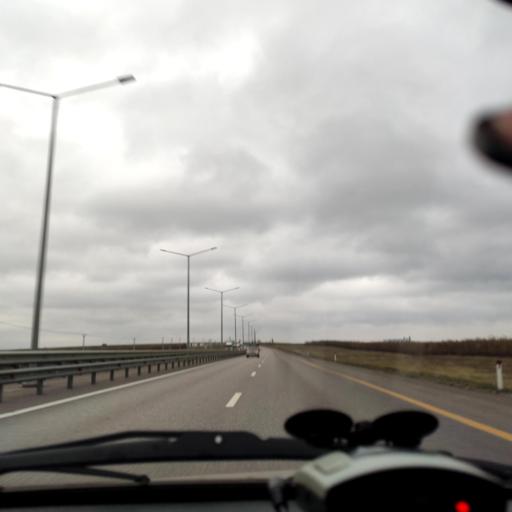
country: RU
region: Voronezj
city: Novaya Usman'
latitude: 51.5950
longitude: 39.3589
